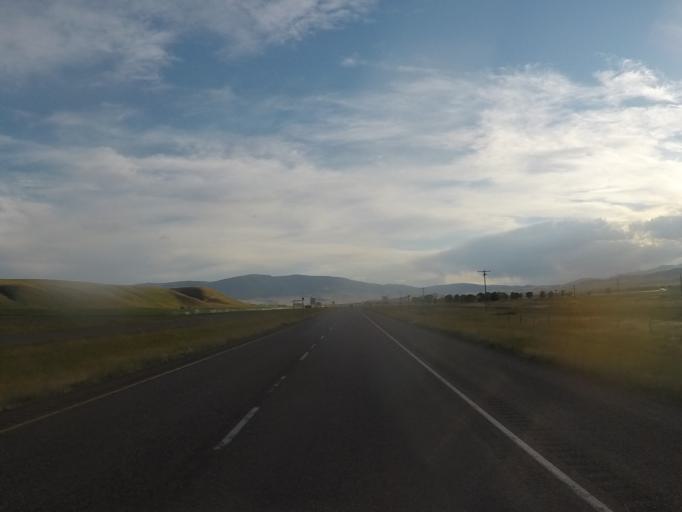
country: US
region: Montana
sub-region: Park County
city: Livingston
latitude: 45.7007
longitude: -110.4704
